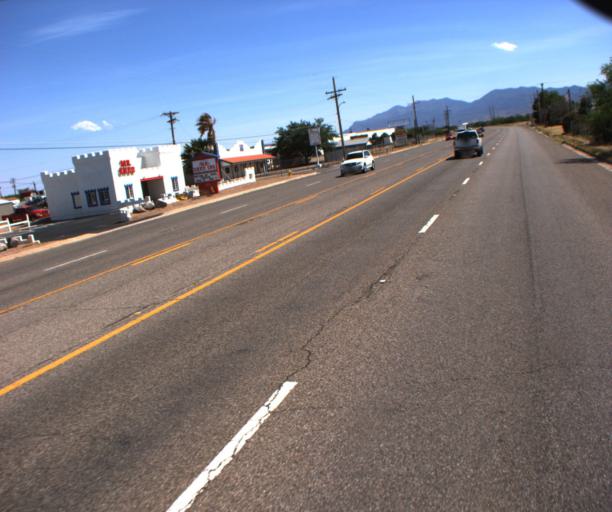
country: US
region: Arizona
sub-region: Cochise County
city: Huachuca City
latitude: 31.6223
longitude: -110.3357
